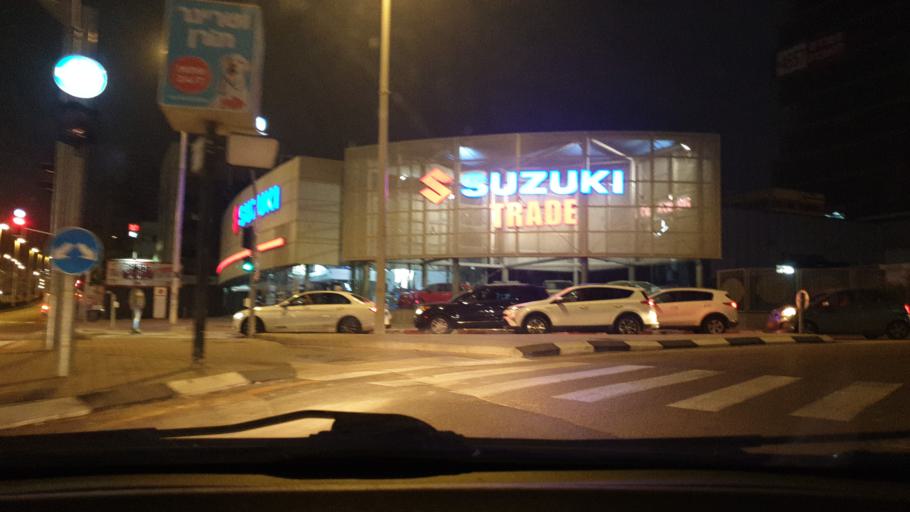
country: IL
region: Tel Aviv
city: Giv`at Shemu'el
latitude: 32.0925
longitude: 34.8536
